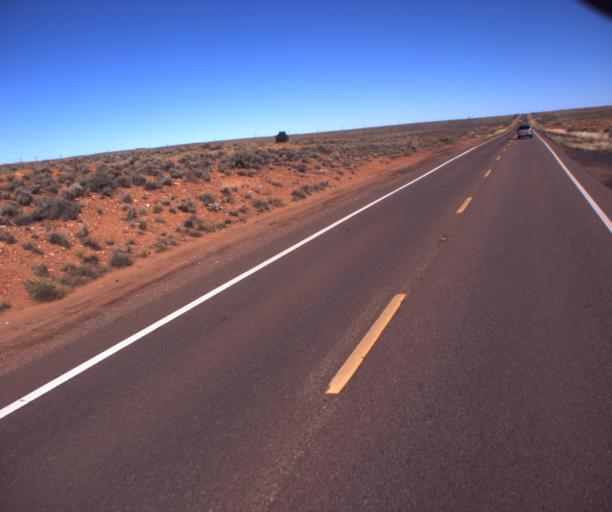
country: US
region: Arizona
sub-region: Navajo County
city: Holbrook
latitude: 34.7740
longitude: -110.1283
